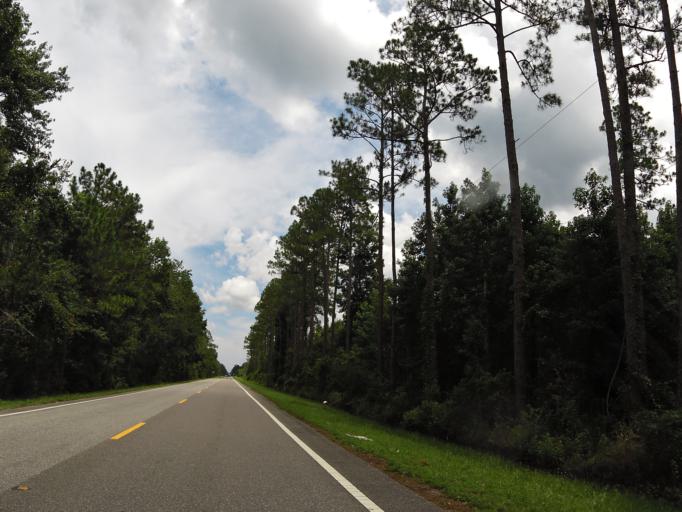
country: US
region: Florida
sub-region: Saint Johns County
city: Saint Augustine Shores
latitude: 29.6514
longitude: -81.3836
